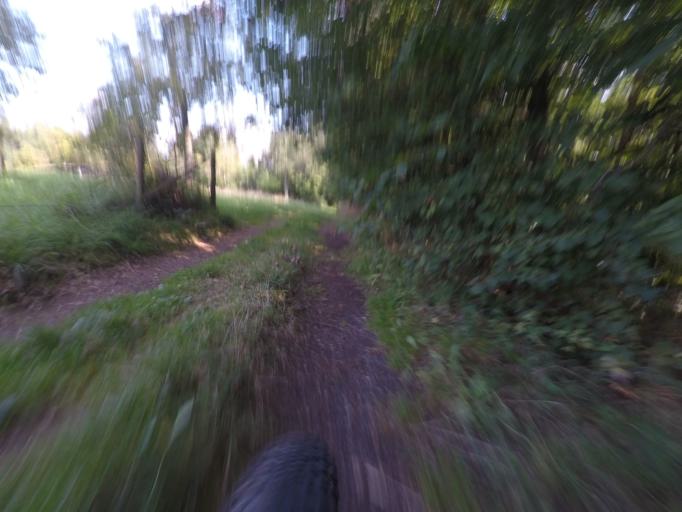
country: DE
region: Baden-Wuerttemberg
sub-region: Regierungsbezirk Stuttgart
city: Steinenbronn
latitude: 48.6657
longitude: 9.1107
